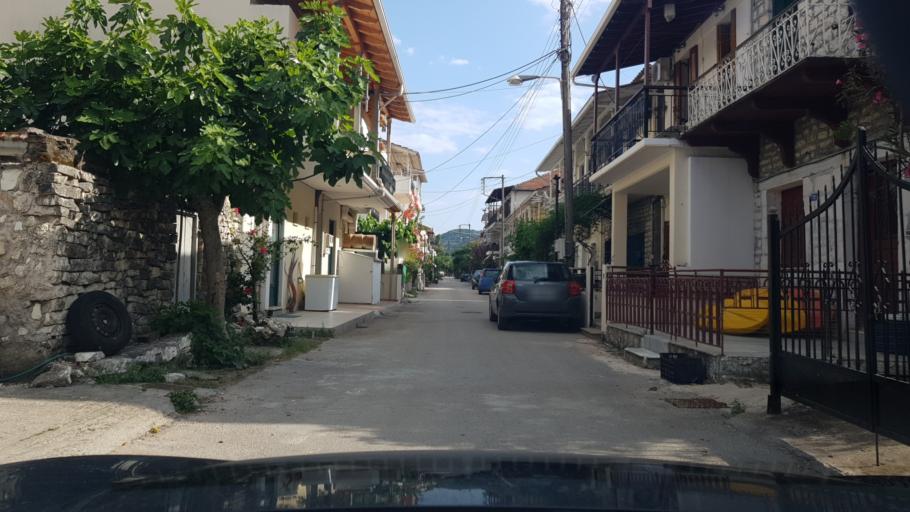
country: GR
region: Ionian Islands
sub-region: Lefkada
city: Nidri
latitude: 38.6864
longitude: 20.6983
